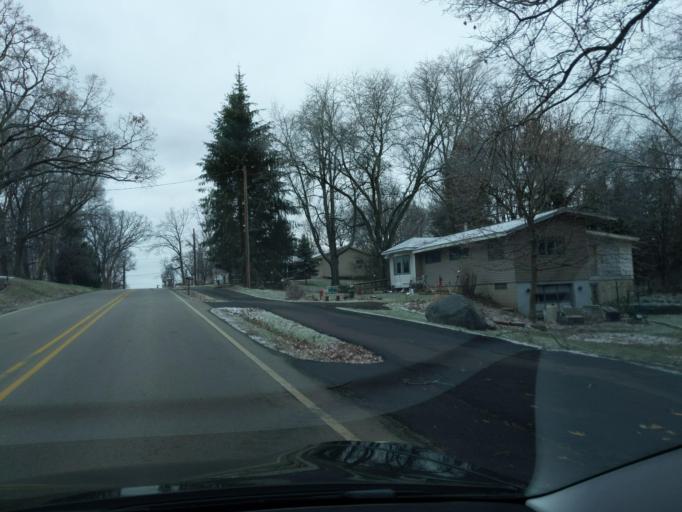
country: US
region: Michigan
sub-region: Jackson County
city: Spring Arbor
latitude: 42.1998
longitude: -84.5537
